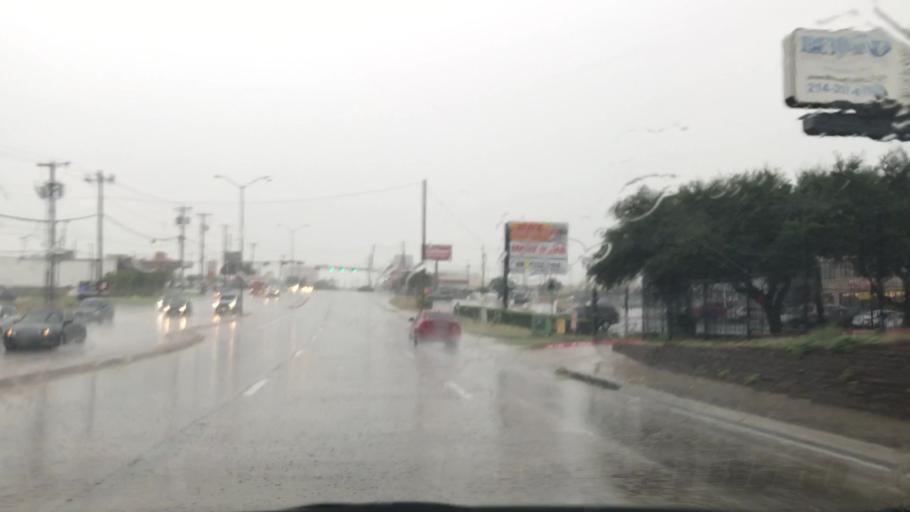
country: US
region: Texas
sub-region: Dallas County
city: Addison
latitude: 32.9348
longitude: -96.8039
